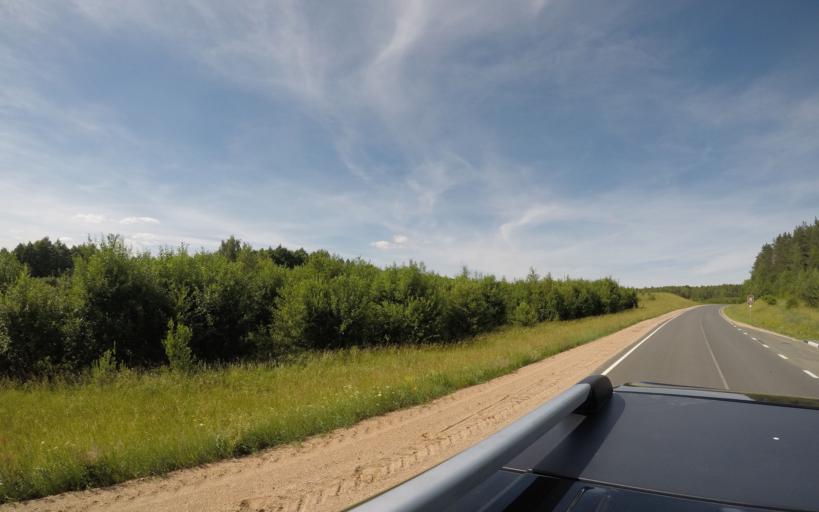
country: BY
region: Grodnenskaya
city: Hal'shany
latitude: 54.2720
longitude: 26.0321
